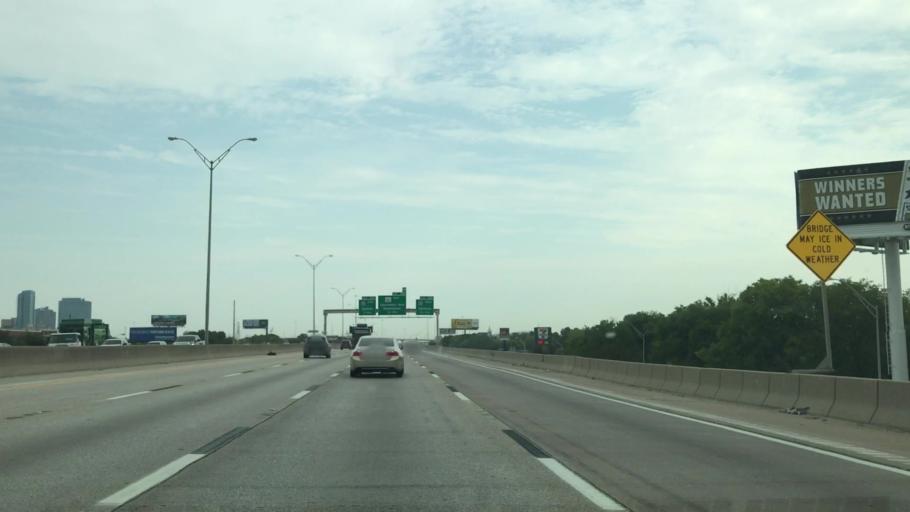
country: US
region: Texas
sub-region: Tarrant County
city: Fort Worth
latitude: 32.7307
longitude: -97.3203
